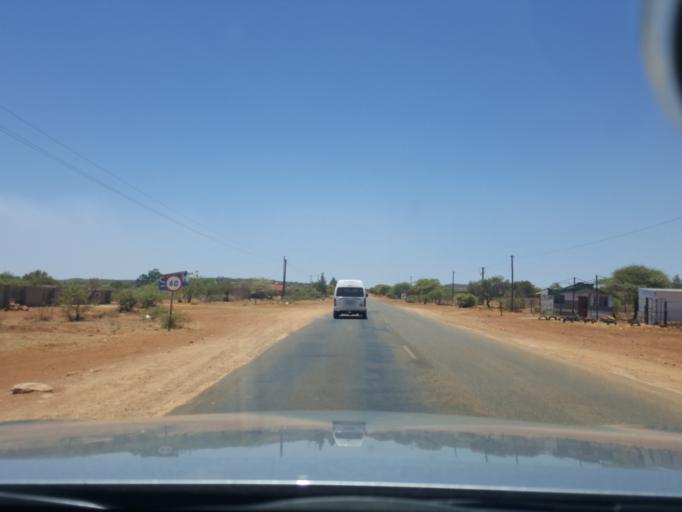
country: ZA
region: North-West
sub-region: Ngaka Modiri Molema District Municipality
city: Zeerust
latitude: -25.4437
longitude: 25.9647
